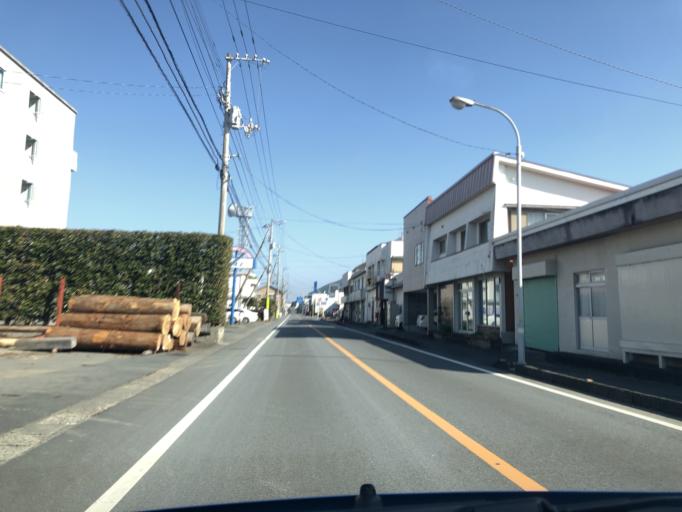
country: JP
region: Kochi
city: Sukumo
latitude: 32.9279
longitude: 132.7104
